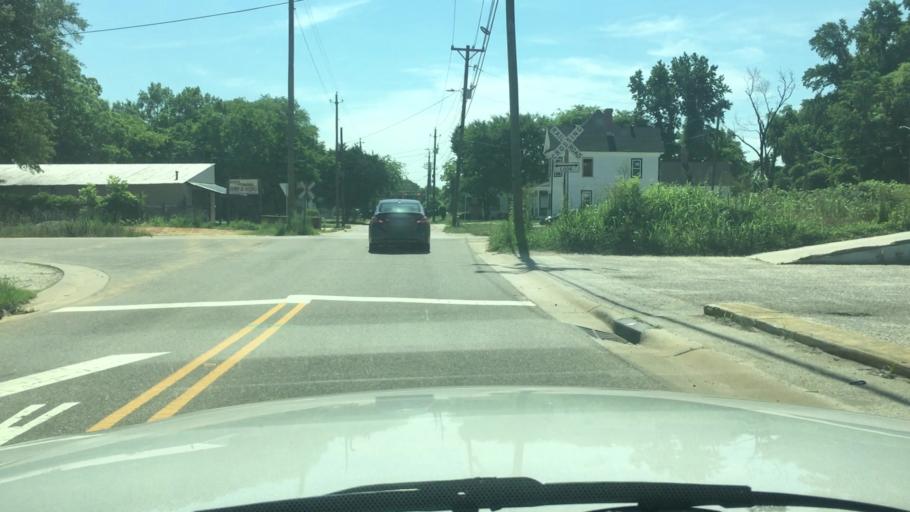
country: US
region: North Carolina
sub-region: Cumberland County
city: Fayetteville
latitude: 35.0469
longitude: -78.8830
